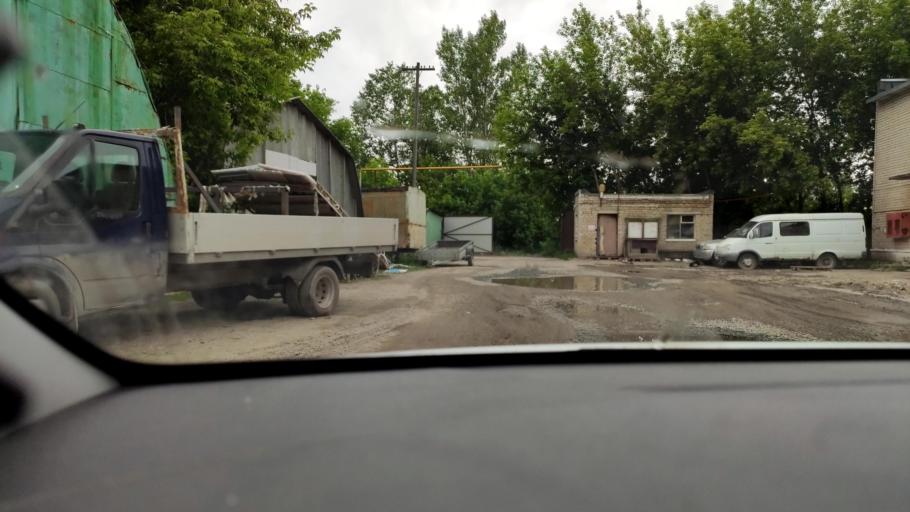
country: RU
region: Tatarstan
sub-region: Gorod Kazan'
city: Kazan
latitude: 55.8514
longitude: 49.1956
